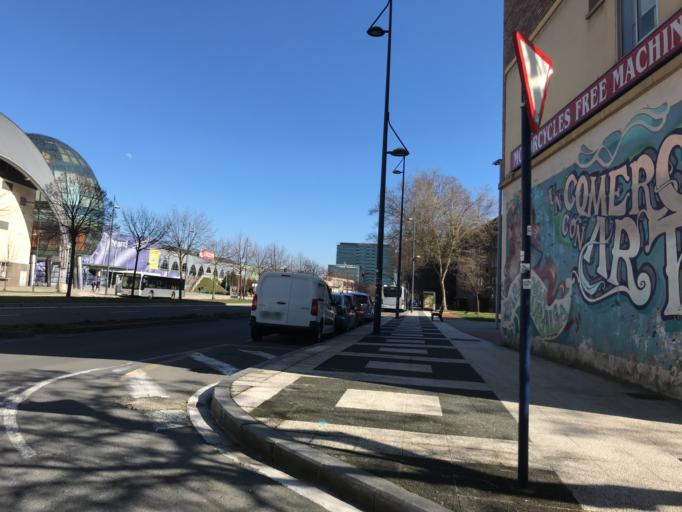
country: ES
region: Basque Country
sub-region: Provincia de Alava
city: Gasteiz / Vitoria
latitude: 42.8611
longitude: -2.6695
